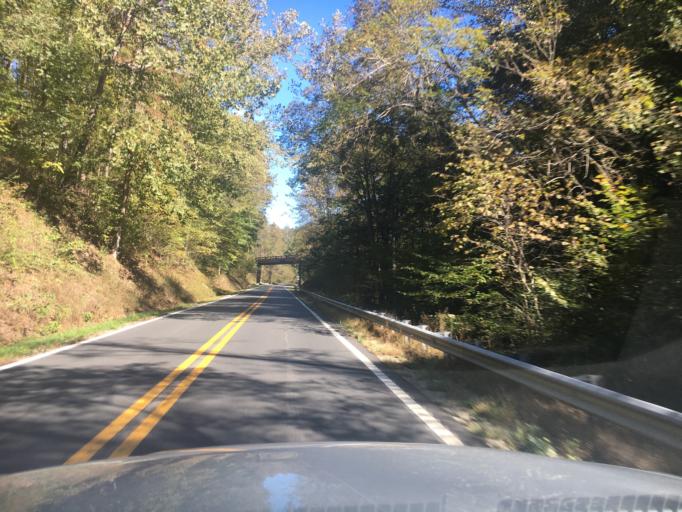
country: US
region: North Carolina
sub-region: Burke County
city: Glen Alpine
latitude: 35.5724
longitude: -81.8467
